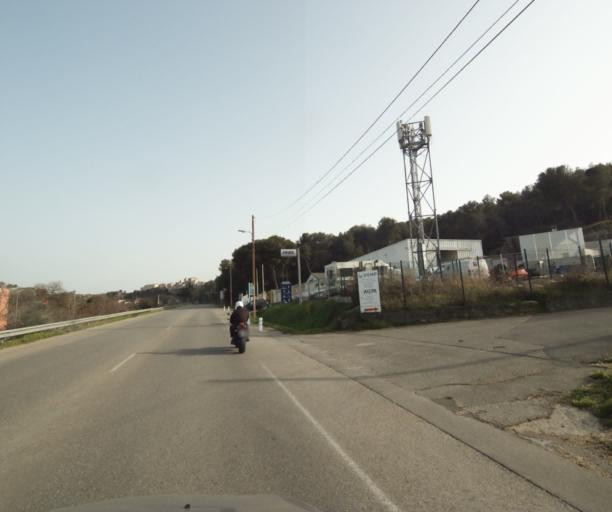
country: FR
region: Provence-Alpes-Cote d'Azur
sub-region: Departement des Bouches-du-Rhone
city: Les Pennes-Mirabeau
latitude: 43.4132
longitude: 5.3011
